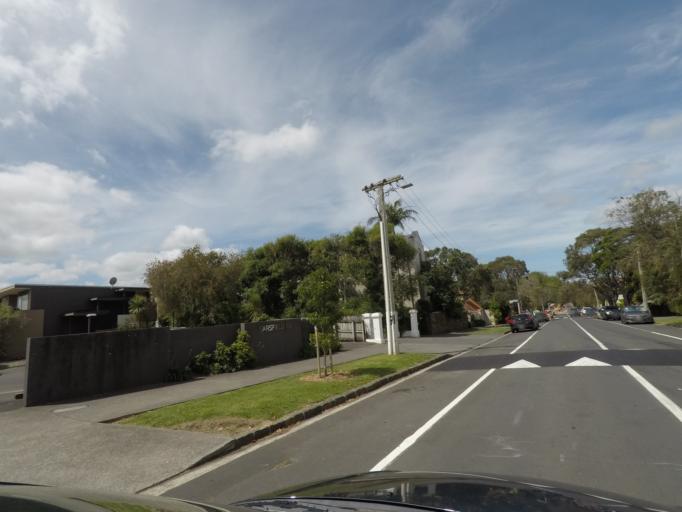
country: NZ
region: Auckland
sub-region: Auckland
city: Auckland
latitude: -36.8412
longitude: 174.7377
